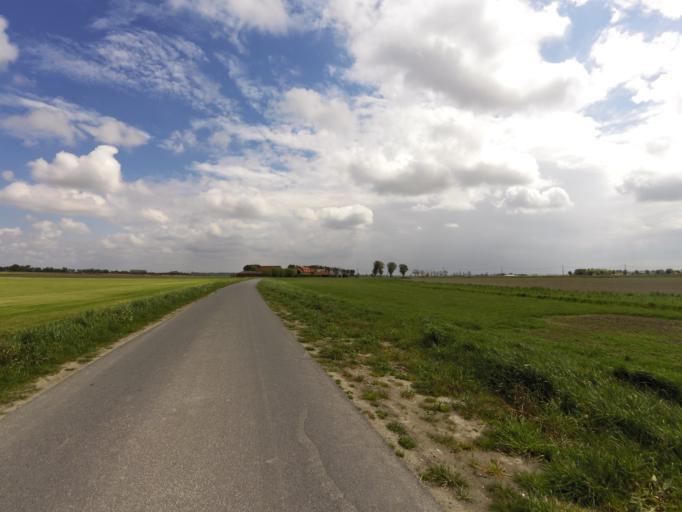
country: BE
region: Flanders
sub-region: Provincie West-Vlaanderen
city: Middelkerke
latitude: 51.1302
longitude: 2.8406
